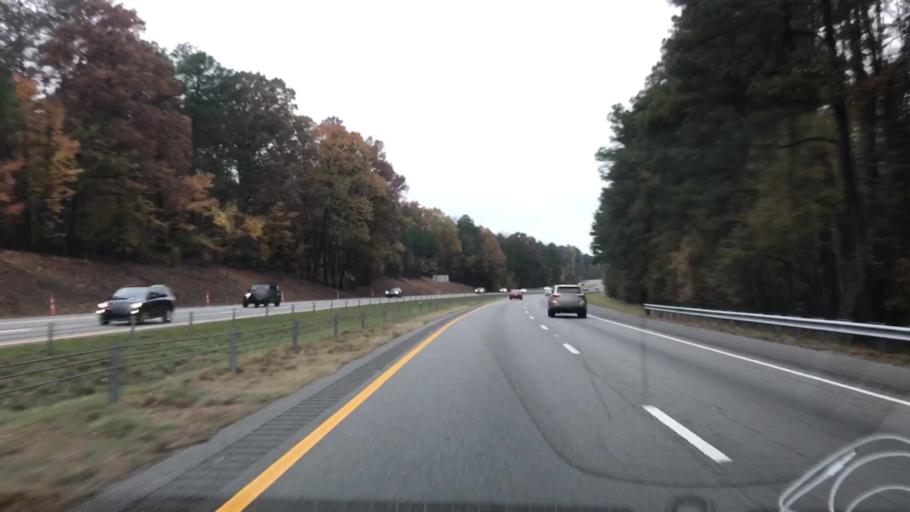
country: US
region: South Carolina
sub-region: Newberry County
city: Prosperity
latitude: 34.2419
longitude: -81.4693
